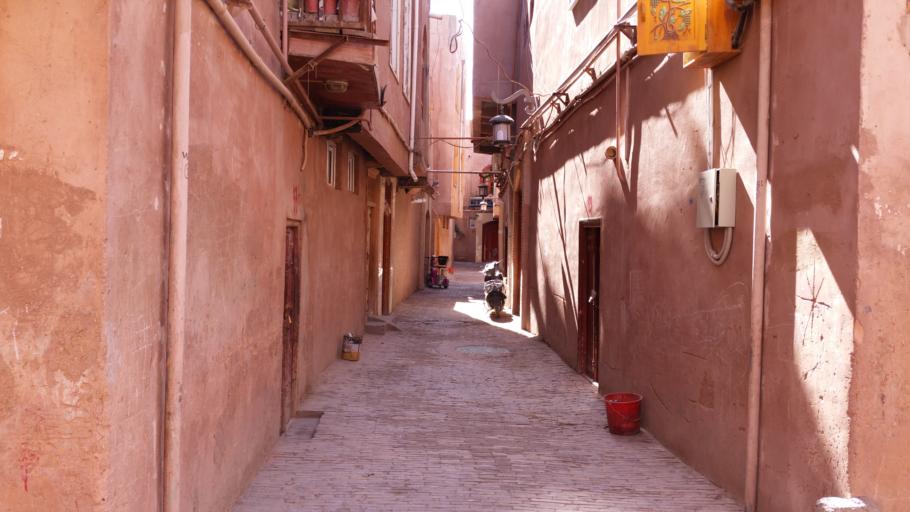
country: CN
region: Xinjiang Uygur Zizhiqu
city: Kashi
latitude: 39.4683
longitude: 75.9811
